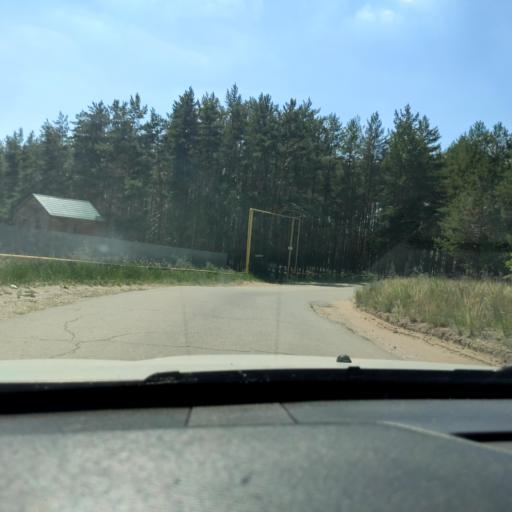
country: RU
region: Samara
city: Pribrezhnyy
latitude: 53.4824
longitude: 49.8340
